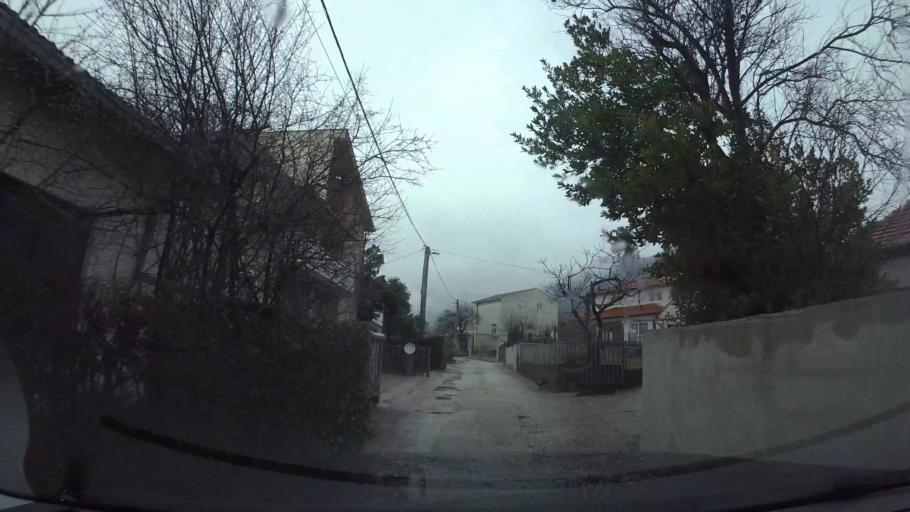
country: BA
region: Federation of Bosnia and Herzegovina
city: Cim
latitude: 43.3497
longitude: 17.7856
